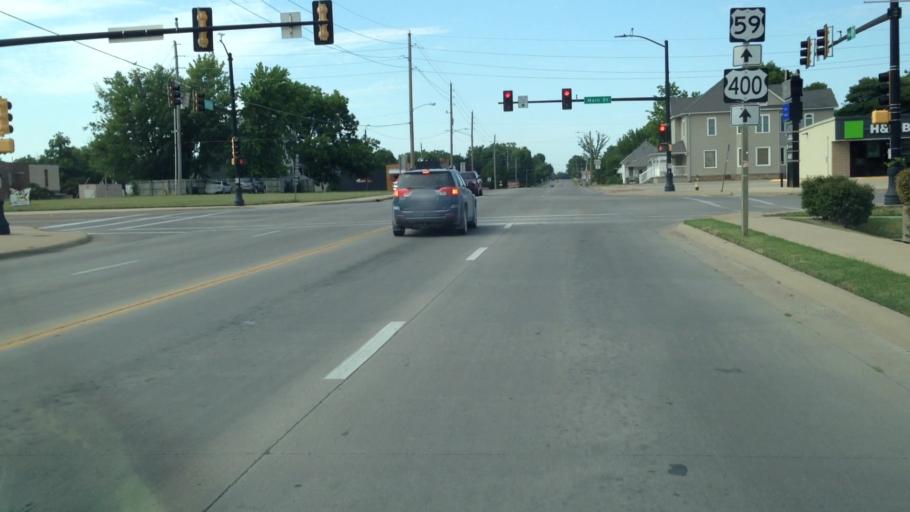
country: US
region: Kansas
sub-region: Labette County
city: Parsons
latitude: 37.3401
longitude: -95.2592
